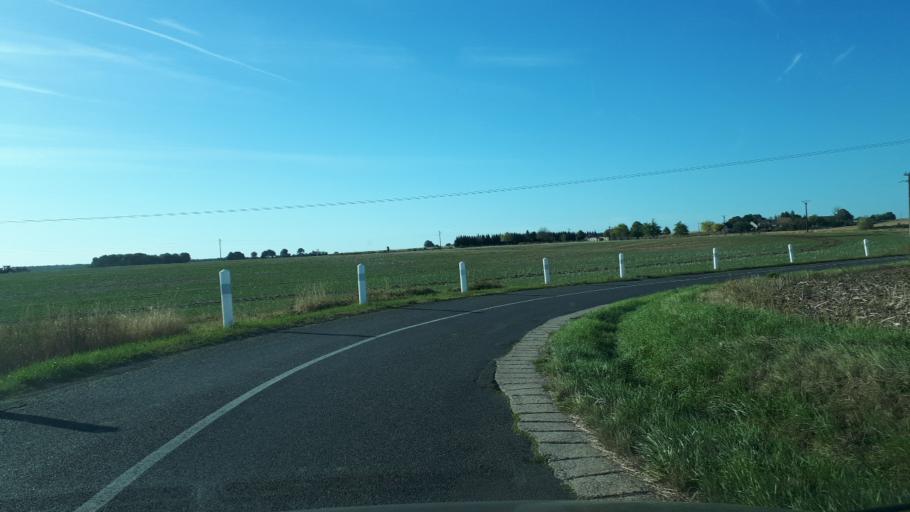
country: FR
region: Centre
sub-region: Departement d'Indre-et-Loire
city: Chateau-Renault
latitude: 47.6441
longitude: 0.9450
